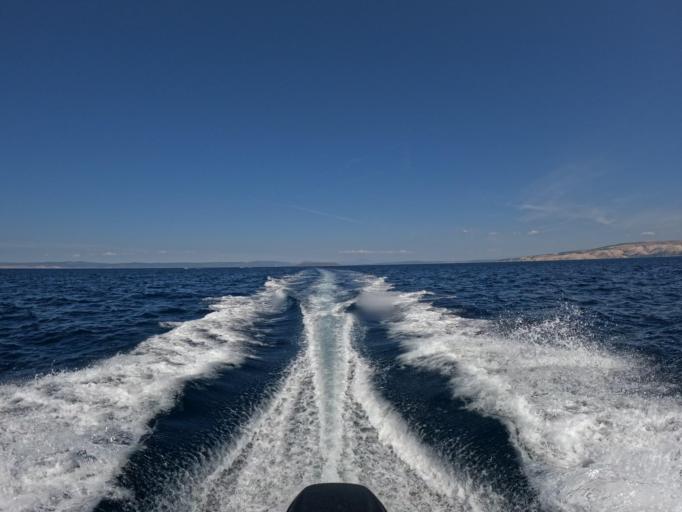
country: HR
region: Primorsko-Goranska
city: Lopar
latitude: 44.8853
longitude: 14.6518
